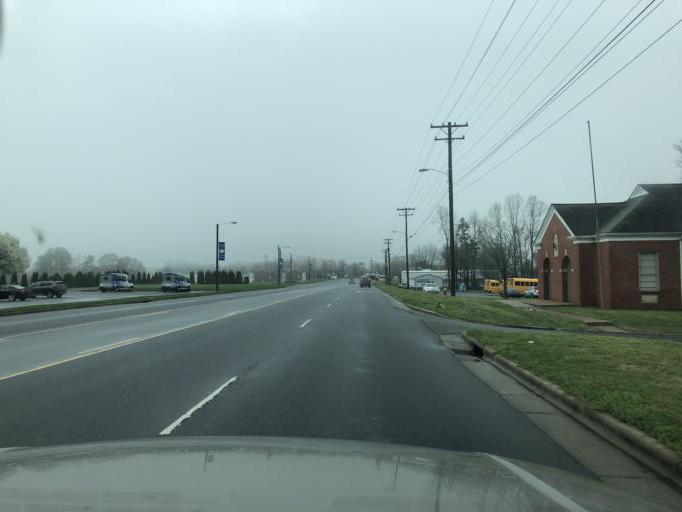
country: US
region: North Carolina
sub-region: Cleveland County
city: Shelby
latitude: 35.2798
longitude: -81.4936
